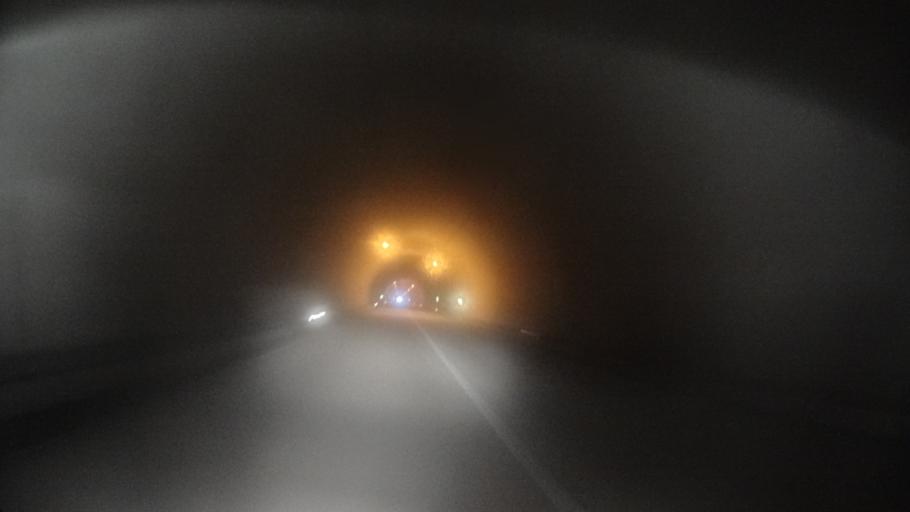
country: JP
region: Fukui
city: Maruoka
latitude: 36.1786
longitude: 136.3397
